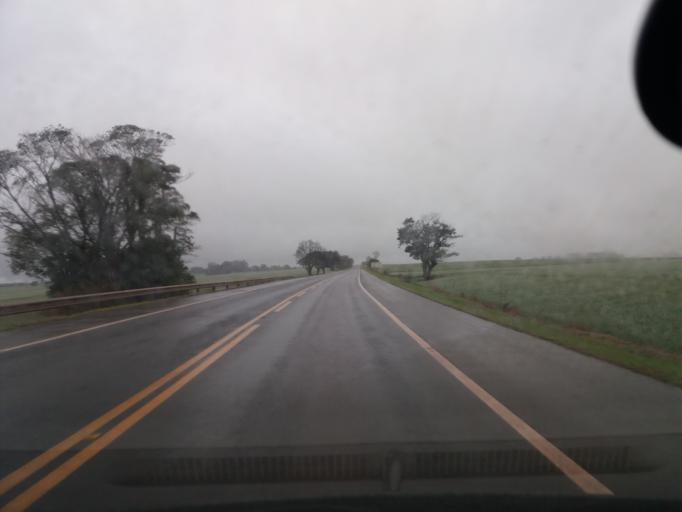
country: BR
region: Parana
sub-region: Campo Mourao
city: Campo Mourao
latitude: -24.3057
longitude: -52.6053
